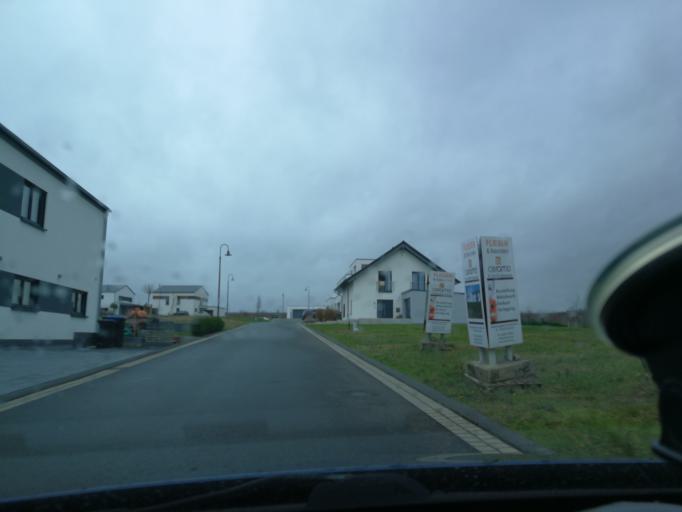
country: DE
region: Rheinland-Pfalz
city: Mehring
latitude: 49.7974
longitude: 6.8167
